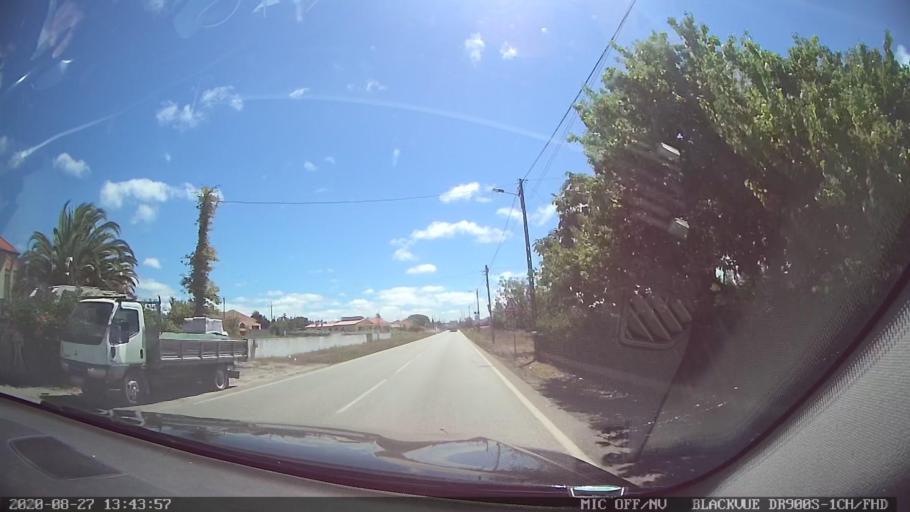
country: PT
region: Coimbra
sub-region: Mira
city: Mira
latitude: 40.4163
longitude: -8.7364
